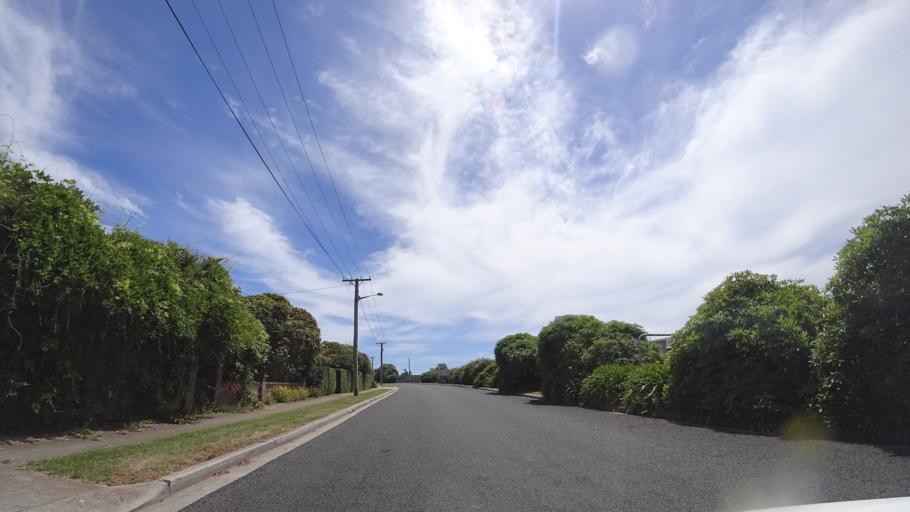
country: AU
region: Tasmania
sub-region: Dorset
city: Scottsdale
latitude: -41.1625
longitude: 147.5138
